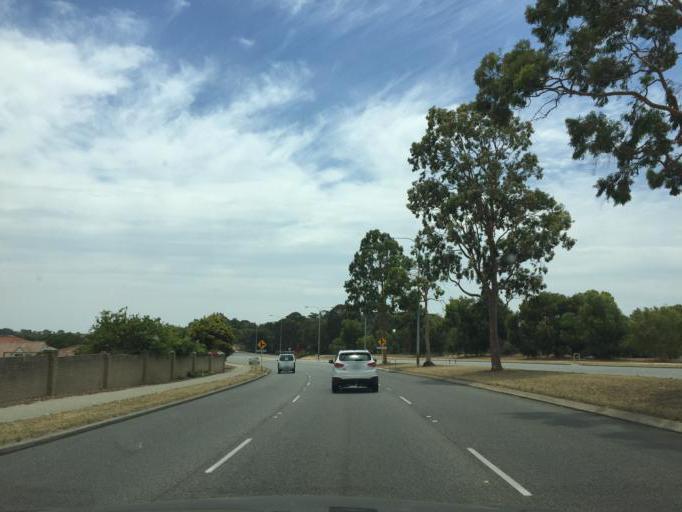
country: AU
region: Western Australia
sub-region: Melville
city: Kardinya
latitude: -32.0683
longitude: 115.8252
